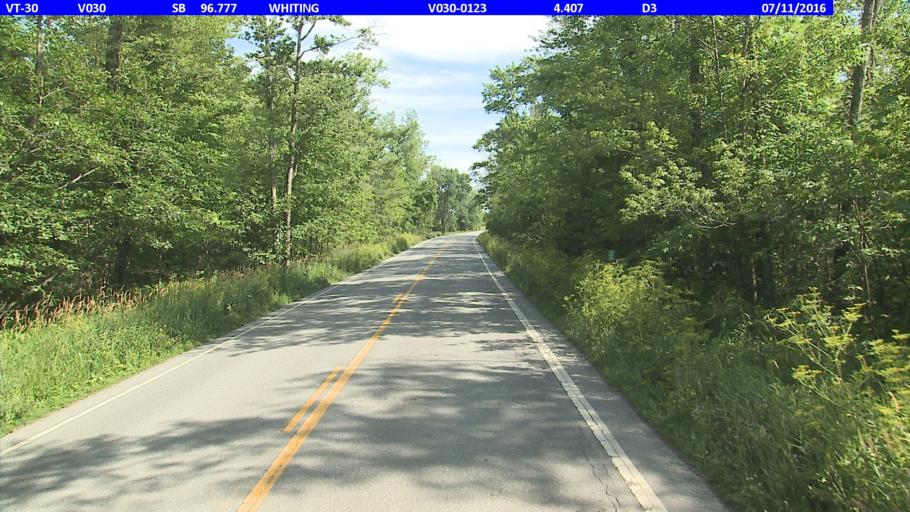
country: US
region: Vermont
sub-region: Addison County
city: Middlebury (village)
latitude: 43.9006
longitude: -73.2056
